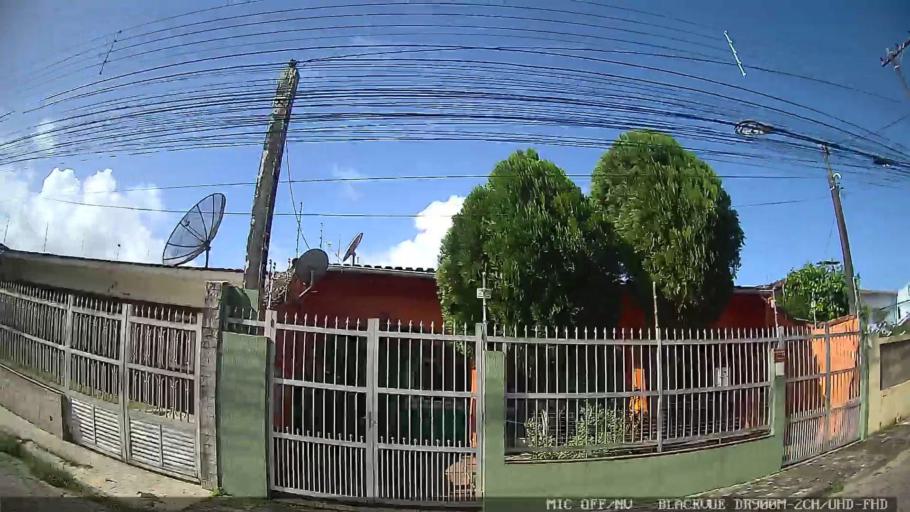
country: BR
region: Sao Paulo
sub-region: Itanhaem
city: Itanhaem
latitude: -24.1615
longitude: -46.7514
